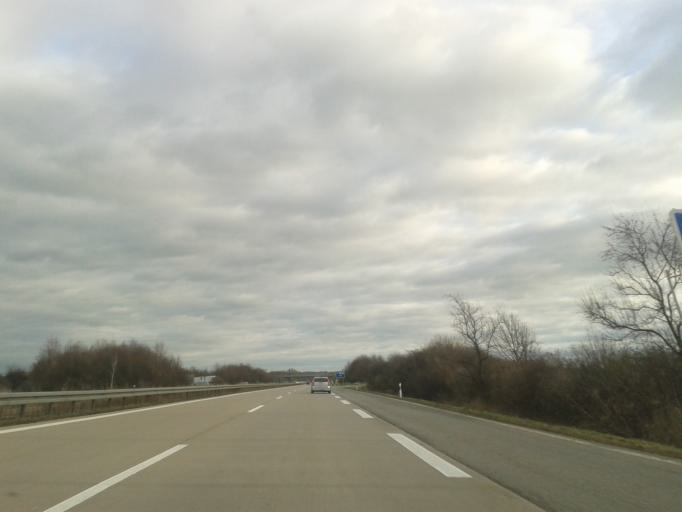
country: DE
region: Saxony
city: Malschwitz
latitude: 51.2105
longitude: 14.5514
